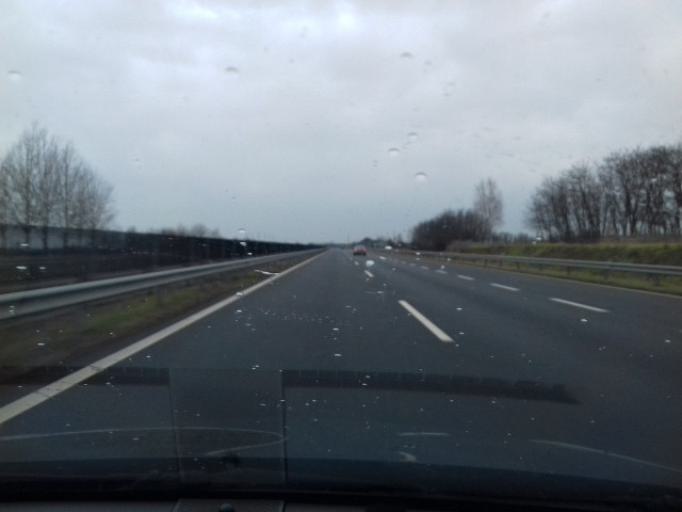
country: HU
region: Szabolcs-Szatmar-Bereg
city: Nyiregyhaza
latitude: 47.8881
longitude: 21.7527
